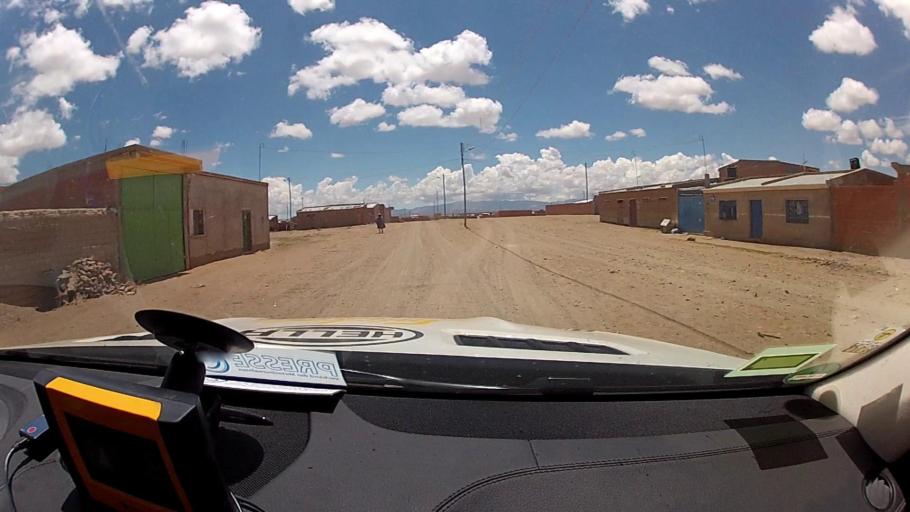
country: BO
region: Potosi
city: Villazon
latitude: -22.0804
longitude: -65.6093
